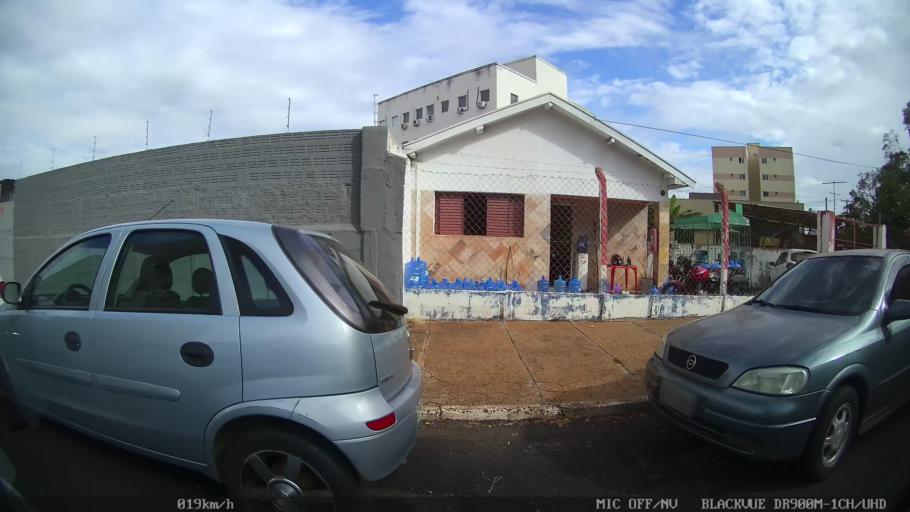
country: BR
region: Sao Paulo
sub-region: Sao Jose Do Rio Preto
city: Sao Jose do Rio Preto
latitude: -20.8305
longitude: -49.3843
